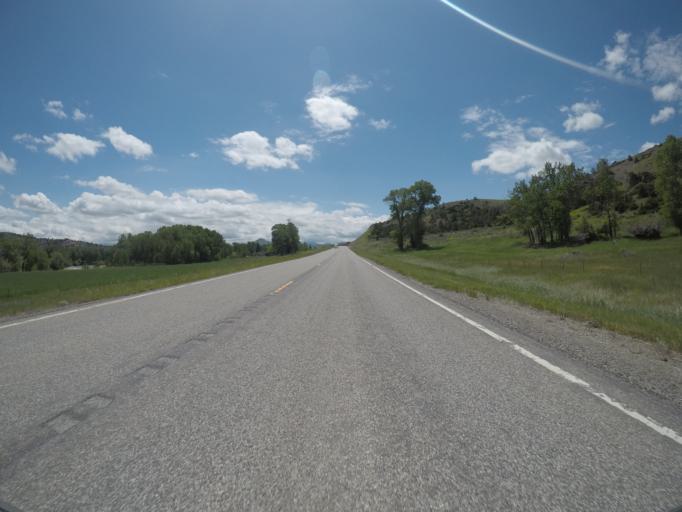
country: US
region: Montana
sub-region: Sweet Grass County
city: Big Timber
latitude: 45.7425
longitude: -109.9964
